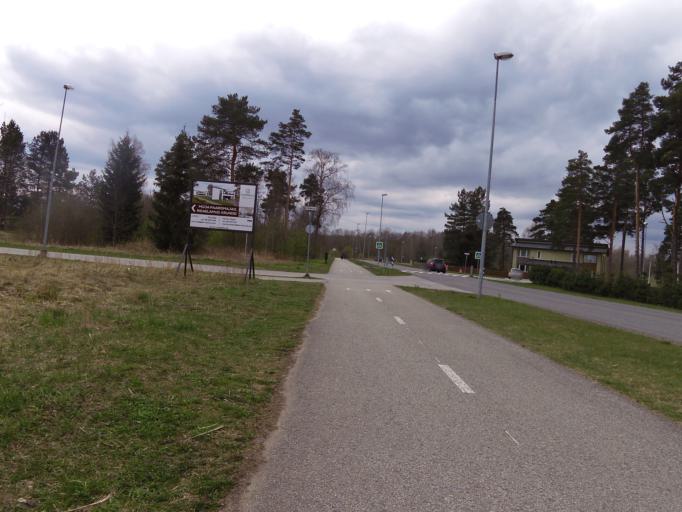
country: EE
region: Harju
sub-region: Kiili vald
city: Kiili
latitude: 59.3594
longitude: 24.8130
